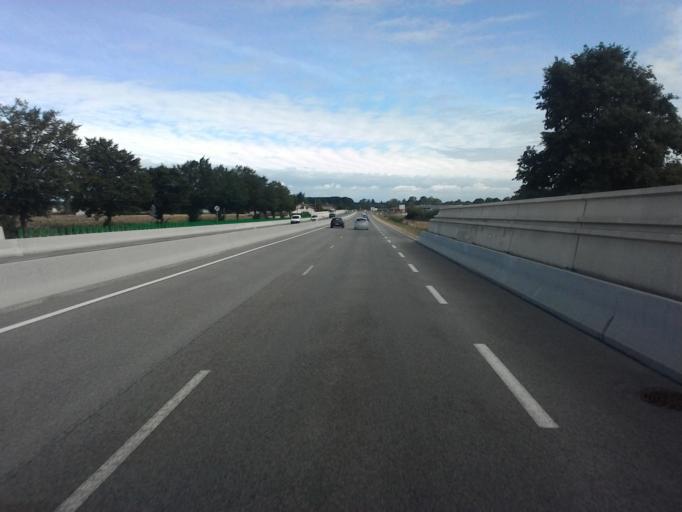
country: FR
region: Rhone-Alpes
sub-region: Departement de l'Ain
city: Certines
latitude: 46.1509
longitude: 5.2782
